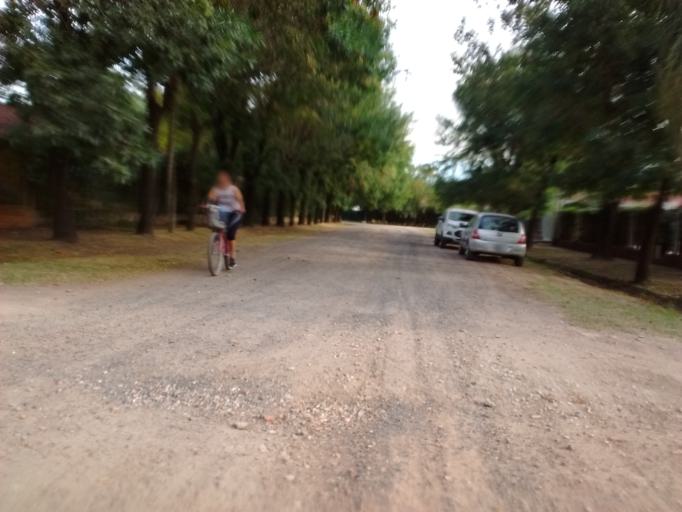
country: AR
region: Santa Fe
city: Funes
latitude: -32.9252
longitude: -60.8082
